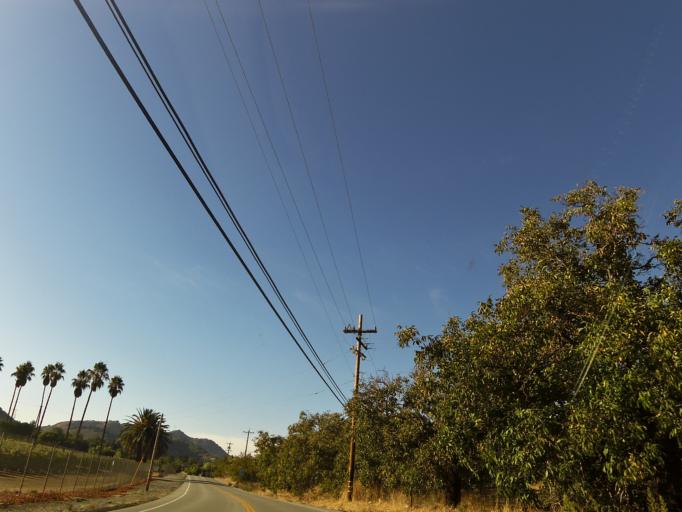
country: US
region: California
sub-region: Santa Clara County
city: San Martin
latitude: 37.0478
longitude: -121.6539
